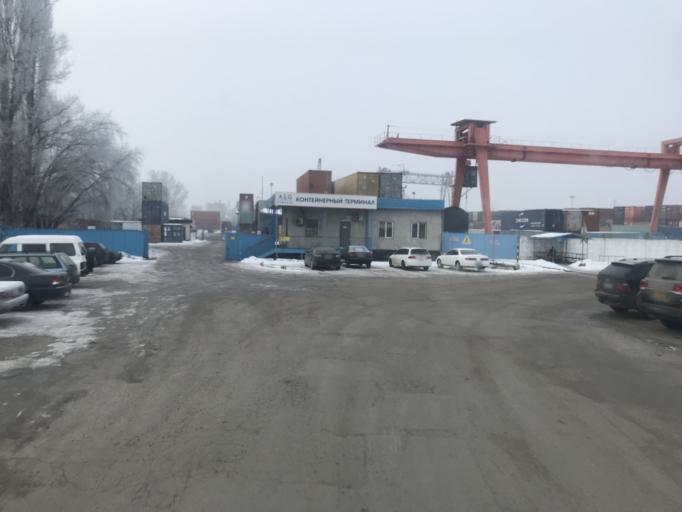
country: KZ
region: Almaty Oblysy
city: Pervomayskiy
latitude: 43.3582
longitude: 76.9731
